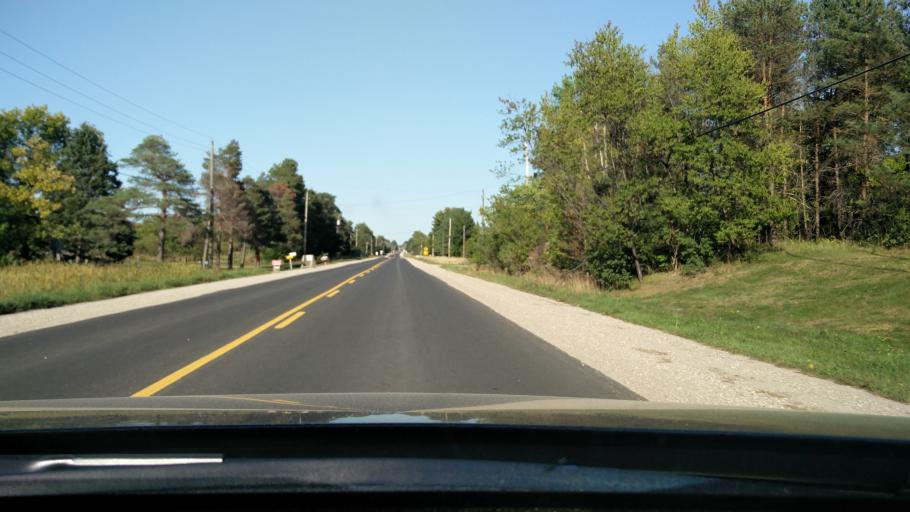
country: CA
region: Ontario
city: Perth
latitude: 44.8759
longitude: -76.2664
